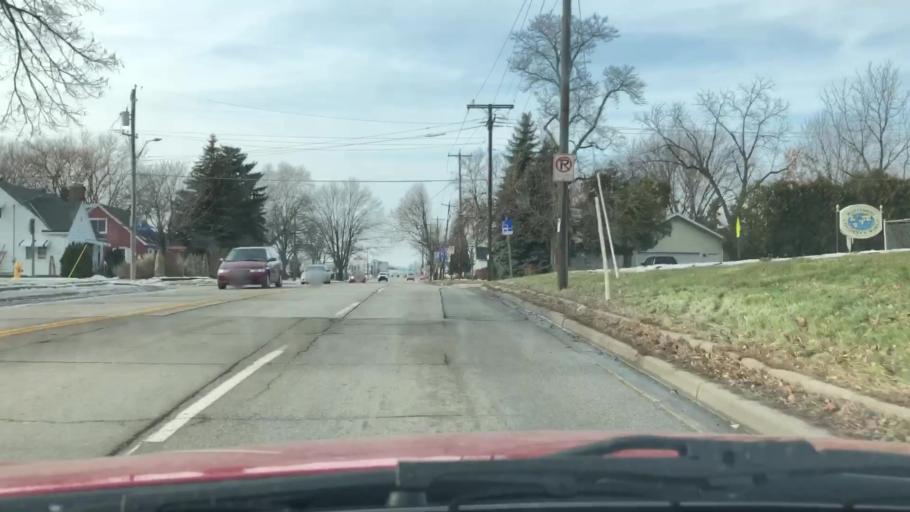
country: US
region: Wisconsin
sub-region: Brown County
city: De Pere
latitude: 44.4486
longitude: -88.0782
